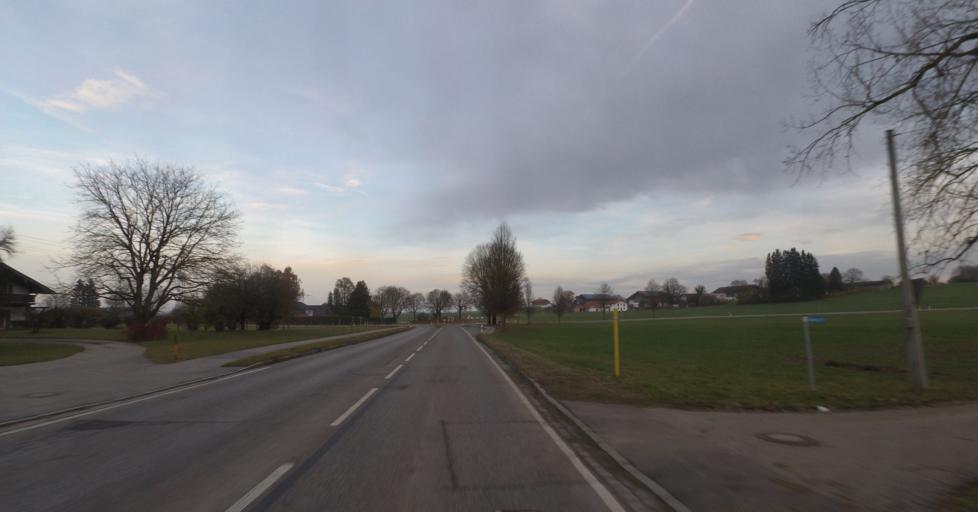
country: DE
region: Bavaria
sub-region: Upper Bavaria
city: Eggstatt
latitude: 47.9097
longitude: 12.3729
